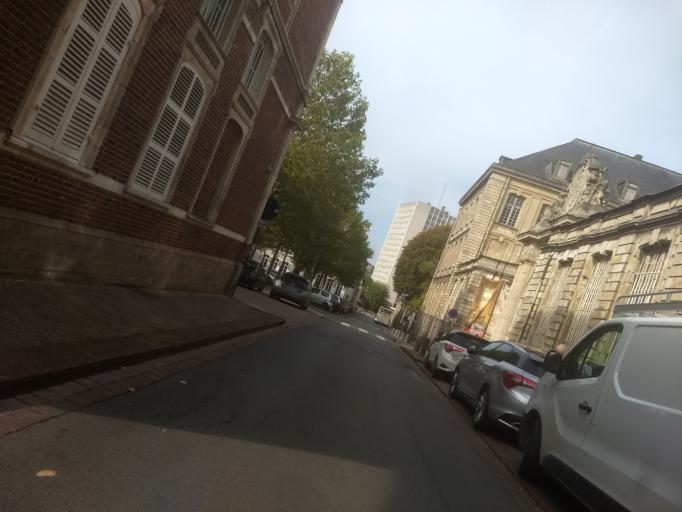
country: FR
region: Nord-Pas-de-Calais
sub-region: Departement du Pas-de-Calais
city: Arras
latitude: 50.2915
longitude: 2.7735
